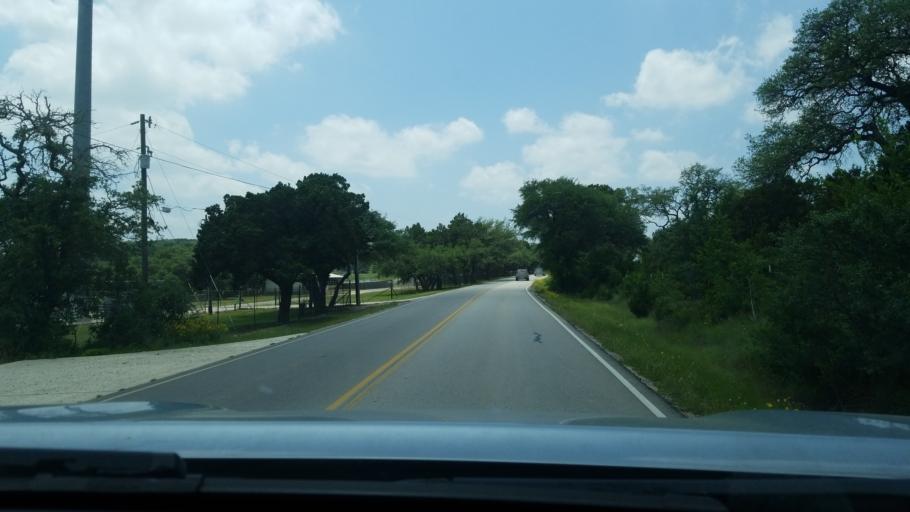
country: US
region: Texas
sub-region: Hays County
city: Woodcreek
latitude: 30.0438
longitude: -98.1062
